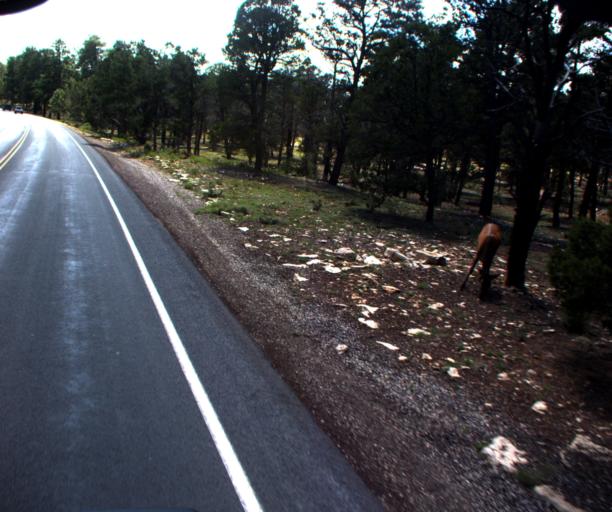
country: US
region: Arizona
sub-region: Coconino County
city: Grand Canyon
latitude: 36.0448
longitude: -112.1188
